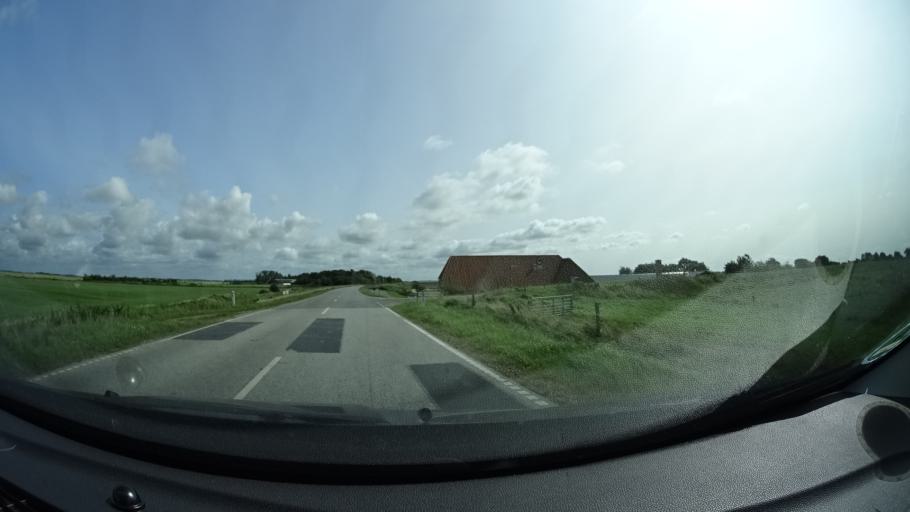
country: DE
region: Schleswig-Holstein
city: Rodenas
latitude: 54.9300
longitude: 8.7198
